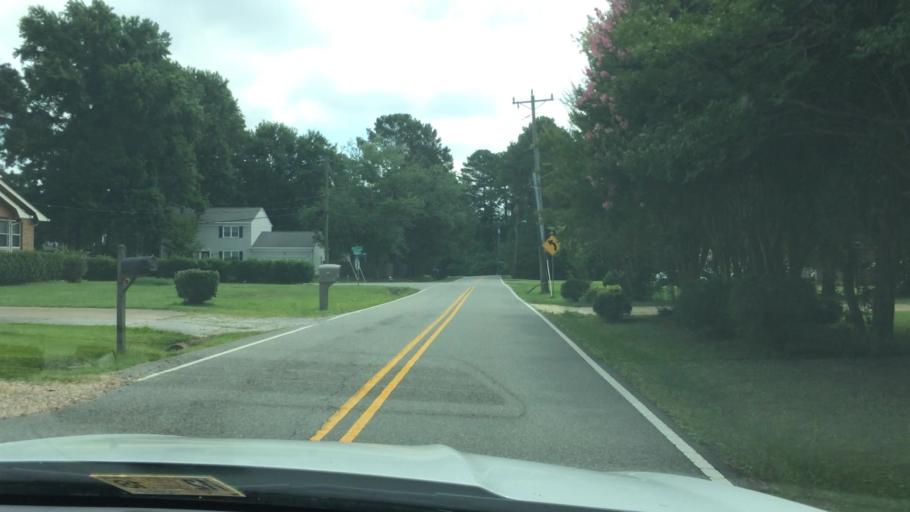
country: US
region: Virginia
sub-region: City of Poquoson
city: Poquoson
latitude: 37.1381
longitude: -76.4494
